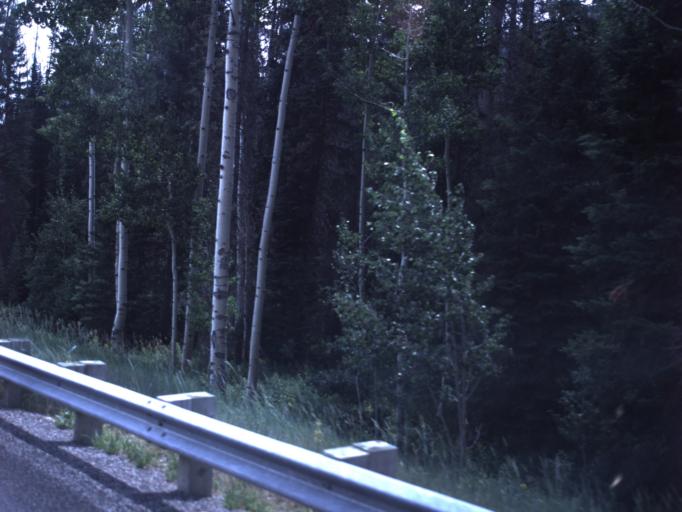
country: US
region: Utah
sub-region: Summit County
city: Francis
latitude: 40.4846
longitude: -110.9524
